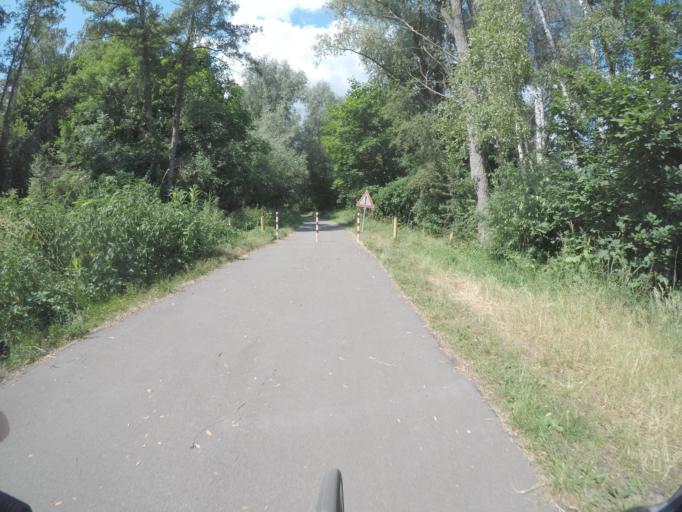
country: DE
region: Brandenburg
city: Roskow
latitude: 52.4428
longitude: 12.7385
